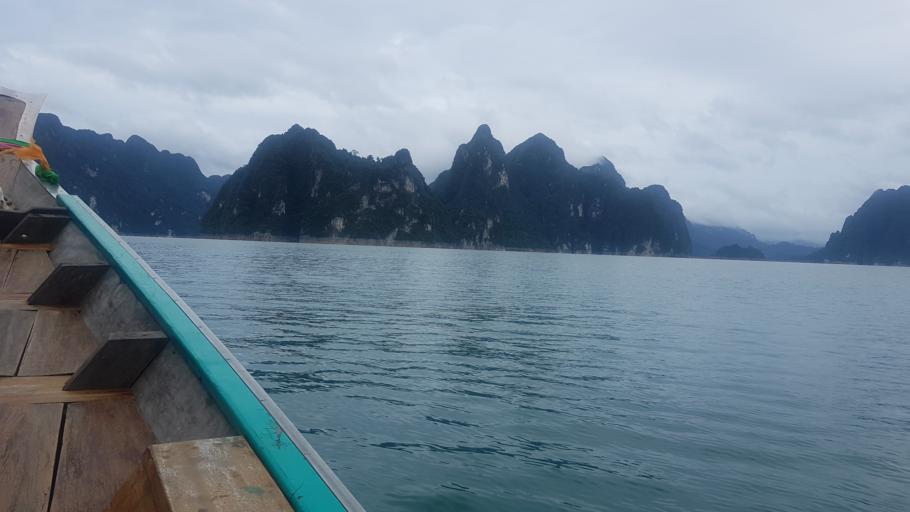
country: TH
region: Surat Thani
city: Phanom
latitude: 9.0340
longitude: 98.7166
